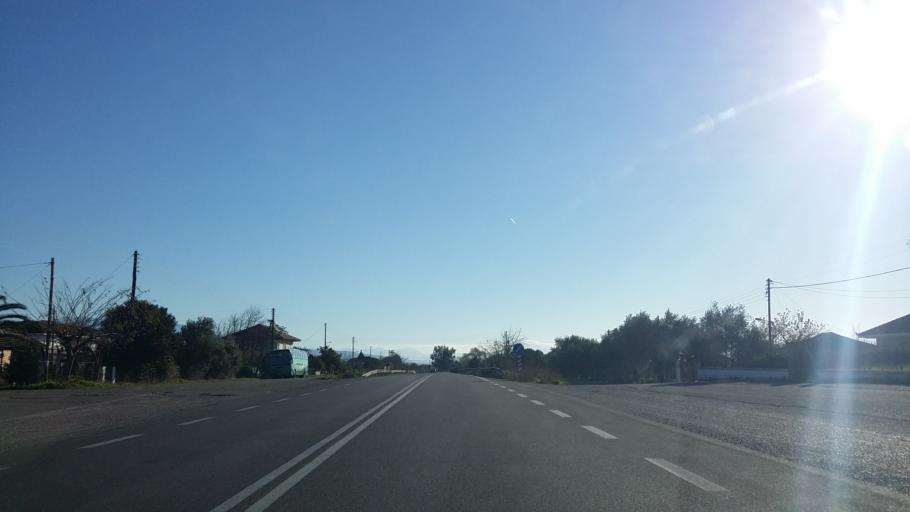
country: GR
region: West Greece
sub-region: Nomos Aitolias kai Akarnanias
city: Fitiai
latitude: 38.6891
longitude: 21.2295
